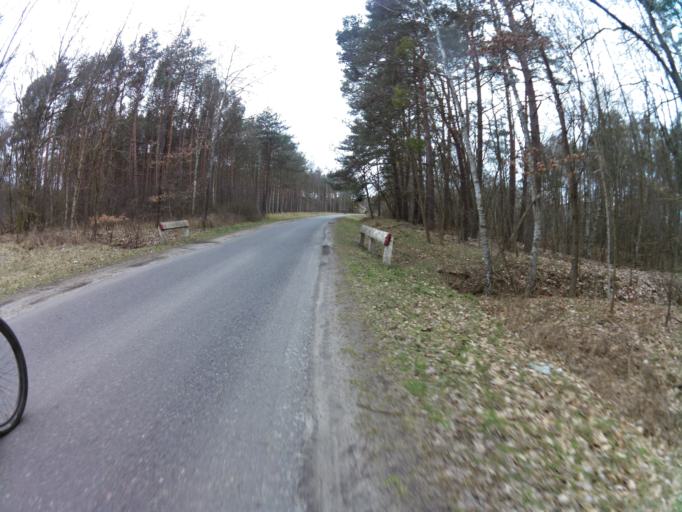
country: PL
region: West Pomeranian Voivodeship
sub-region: Powiat mysliborski
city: Debno
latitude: 52.7436
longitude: 14.7746
